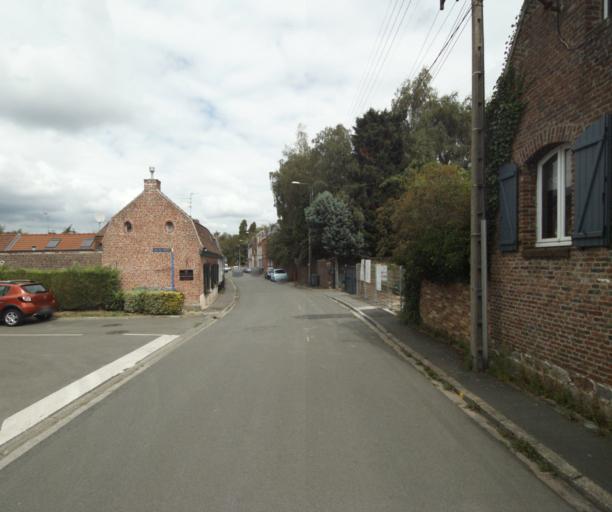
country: FR
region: Nord-Pas-de-Calais
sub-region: Departement du Nord
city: Villeneuve-d'Ascq
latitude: 50.6245
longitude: 3.1536
